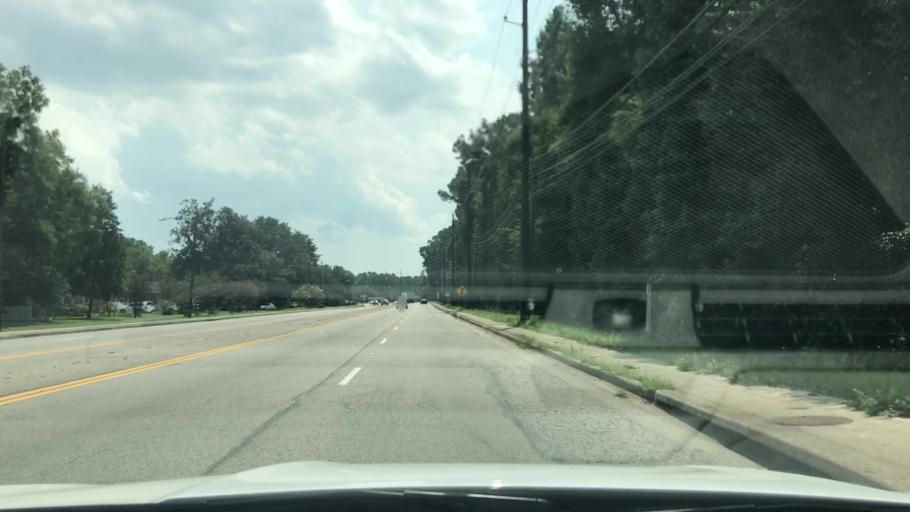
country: US
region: South Carolina
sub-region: Georgetown County
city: Georgetown
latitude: 33.4033
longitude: -79.2885
